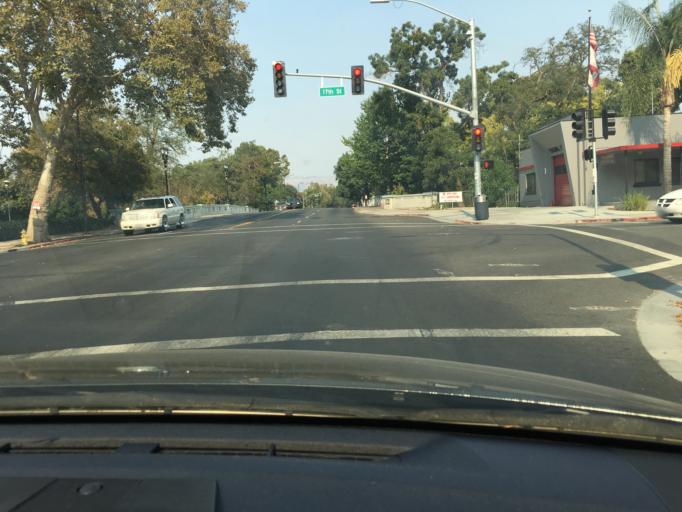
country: US
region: California
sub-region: Santa Clara County
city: San Jose
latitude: 37.3438
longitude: -121.8746
